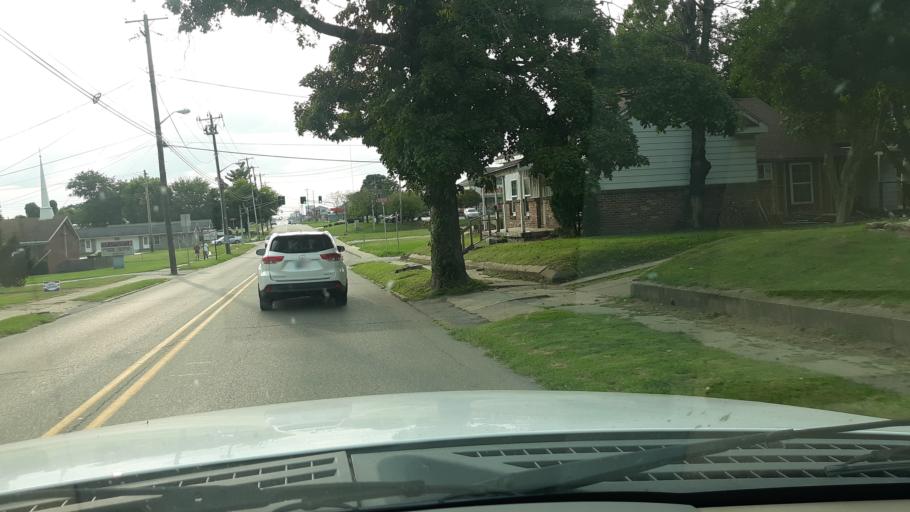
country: US
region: Indiana
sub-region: Gibson County
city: Princeton
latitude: 38.3554
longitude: -87.5764
